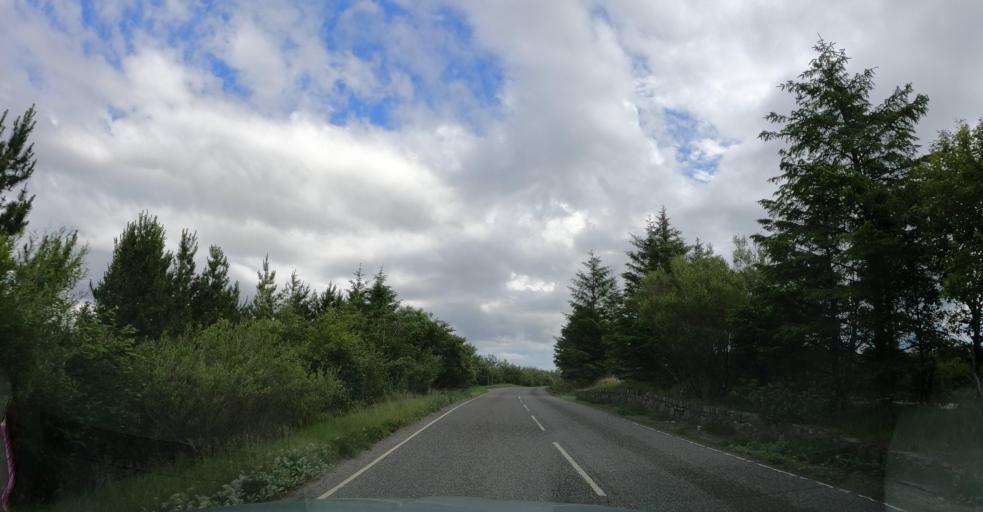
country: GB
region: Scotland
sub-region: Eilean Siar
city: Isle of Lewis
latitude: 58.2111
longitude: -6.4176
